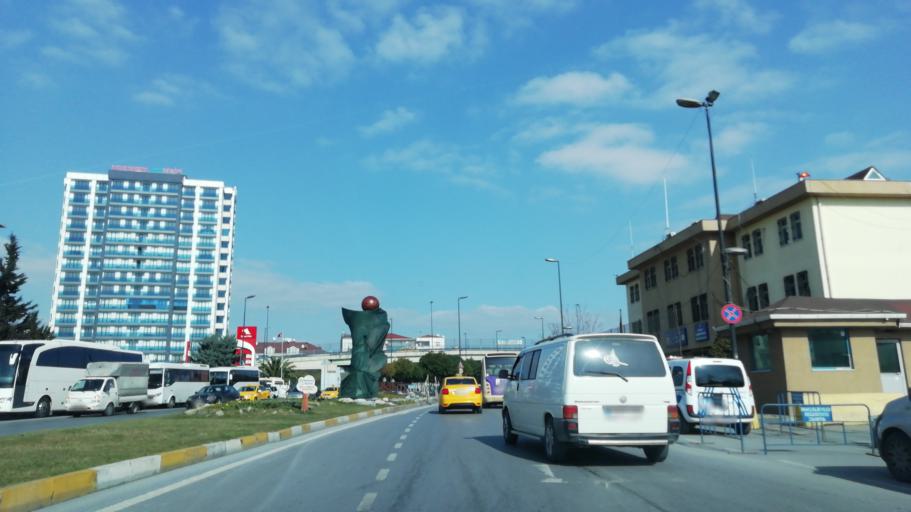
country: TR
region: Istanbul
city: Bahcelievler
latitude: 41.0122
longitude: 28.8473
